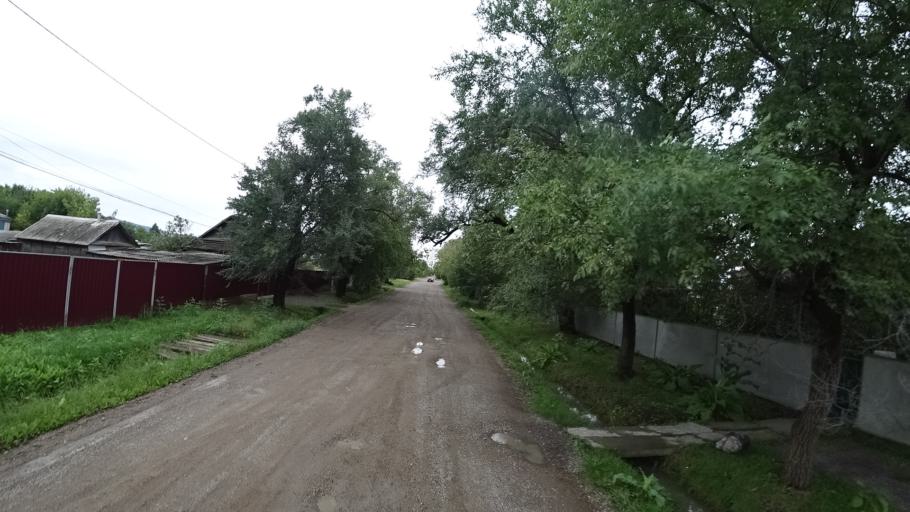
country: RU
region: Primorskiy
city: Chernigovka
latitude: 44.3443
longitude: 132.5676
